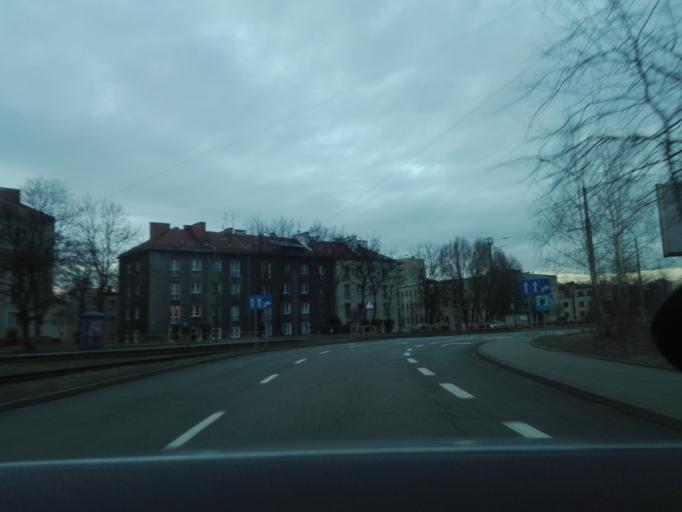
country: PL
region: Silesian Voivodeship
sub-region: Katowice
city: Katowice
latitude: 50.2742
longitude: 19.0247
